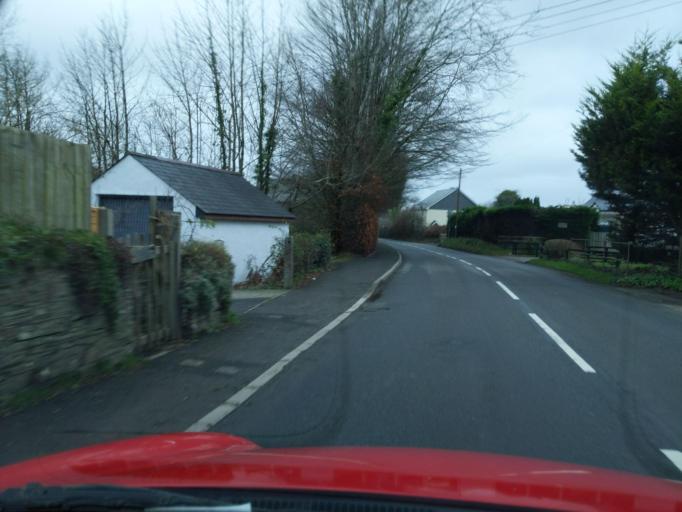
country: GB
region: England
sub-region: Devon
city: Holsworthy
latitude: 50.7679
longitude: -4.3364
